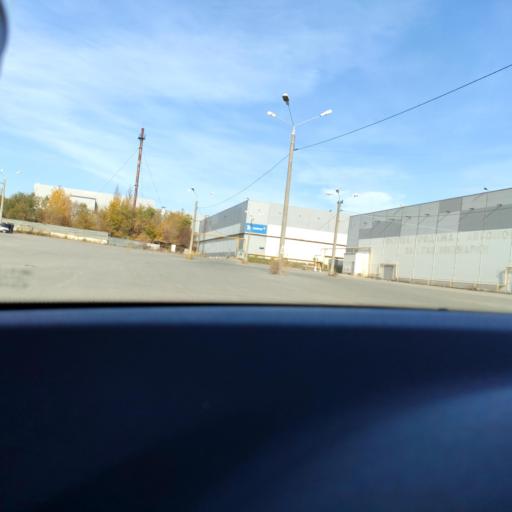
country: RU
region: Samara
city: Petra-Dubrava
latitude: 53.2729
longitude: 50.2736
